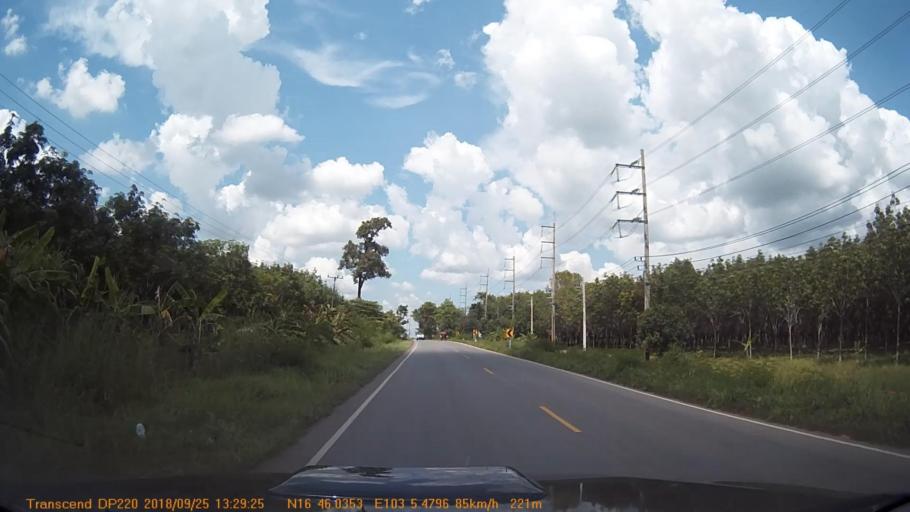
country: TH
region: Khon Kaen
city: Kranuan
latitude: 16.7671
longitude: 103.0913
